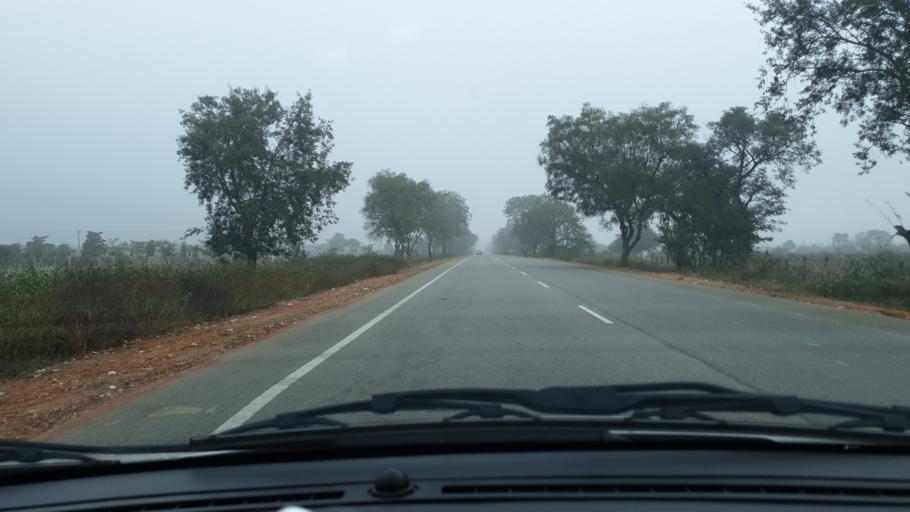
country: IN
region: Telangana
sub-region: Nalgonda
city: Devarkonda
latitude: 16.6341
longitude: 78.6177
